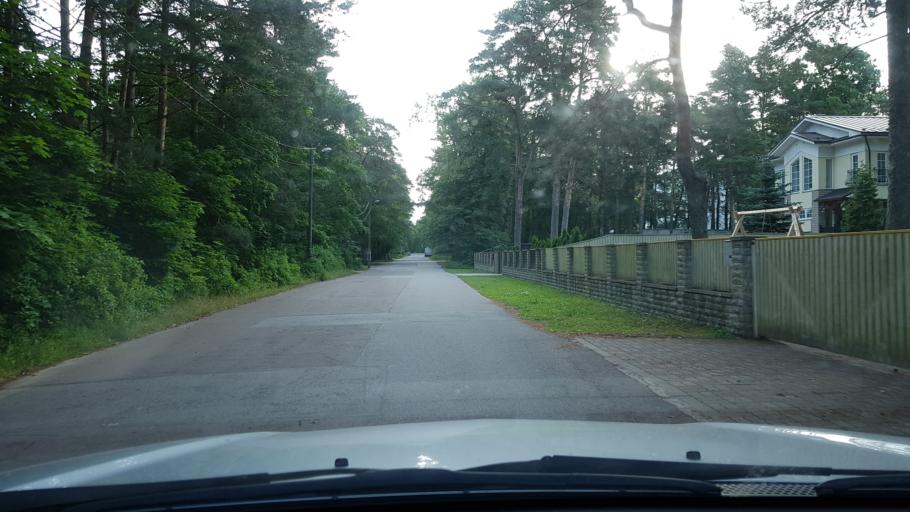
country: EE
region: Ida-Virumaa
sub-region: Narva-Joesuu linn
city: Narva-Joesuu
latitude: 59.4588
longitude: 28.0439
